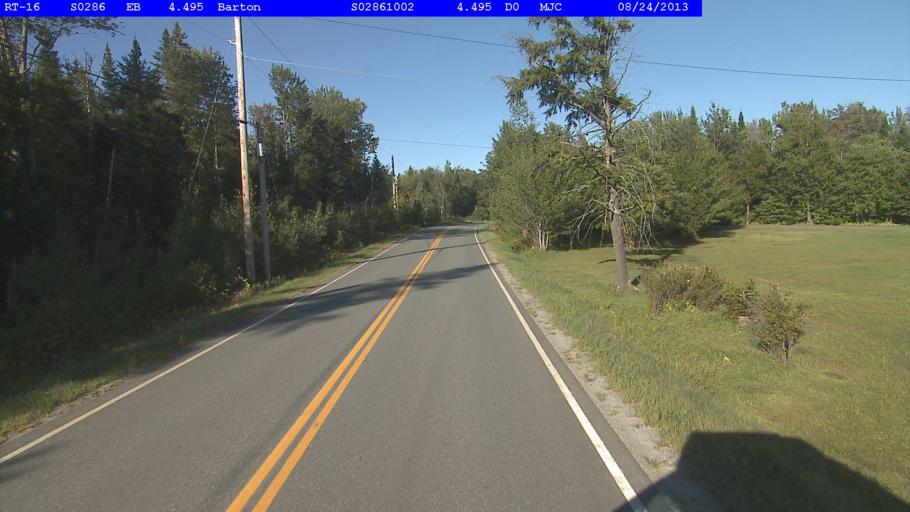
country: US
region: Vermont
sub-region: Orleans County
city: Newport
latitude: 44.7832
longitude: -72.1179
